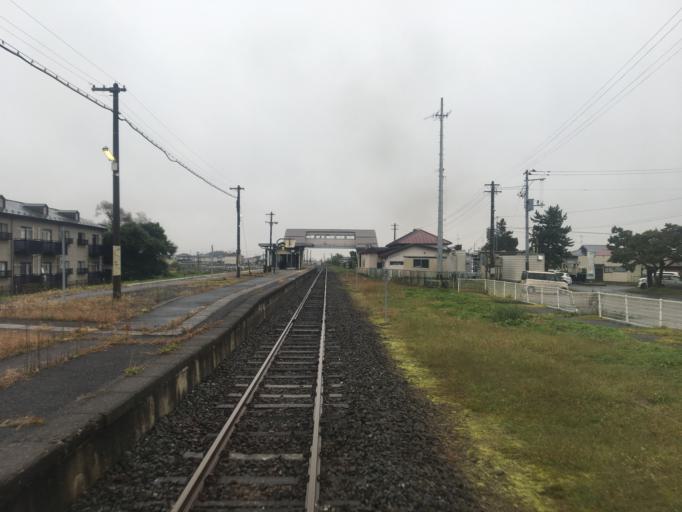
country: JP
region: Miyagi
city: Furukawa
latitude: 38.6529
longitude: 140.8713
